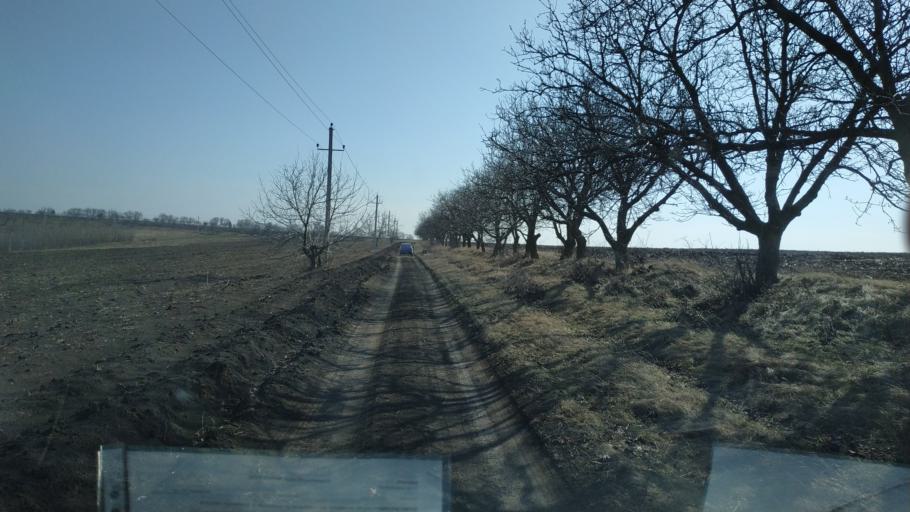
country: MD
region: Causeni
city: Causeni
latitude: 46.5556
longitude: 29.2696
